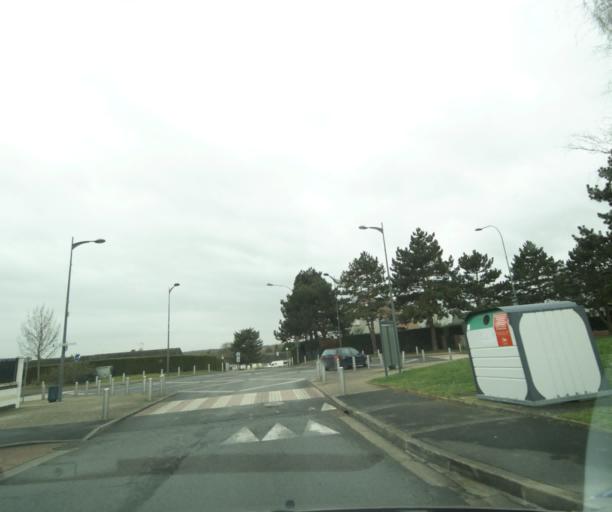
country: FR
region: Picardie
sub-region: Departement de l'Oise
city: Noyon
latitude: 49.5822
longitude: 3.0164
